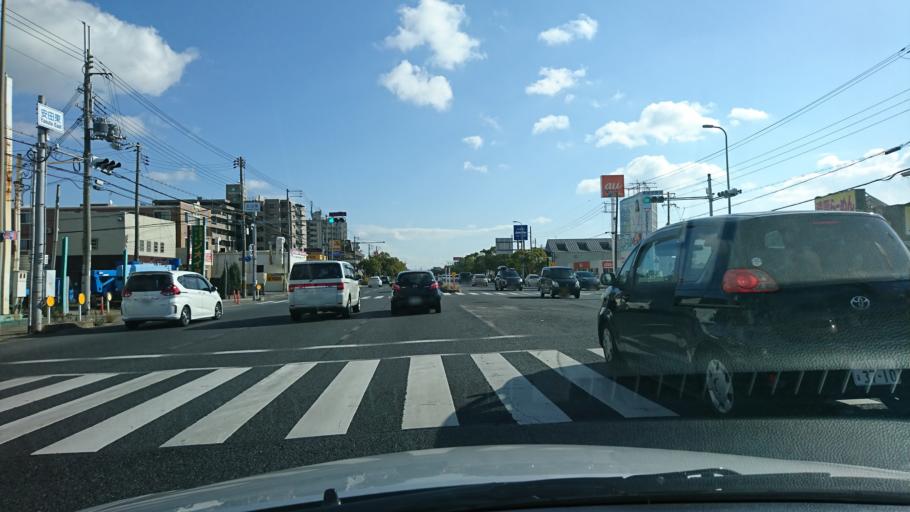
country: JP
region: Hyogo
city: Kakogawacho-honmachi
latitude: 34.7454
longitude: 134.8384
